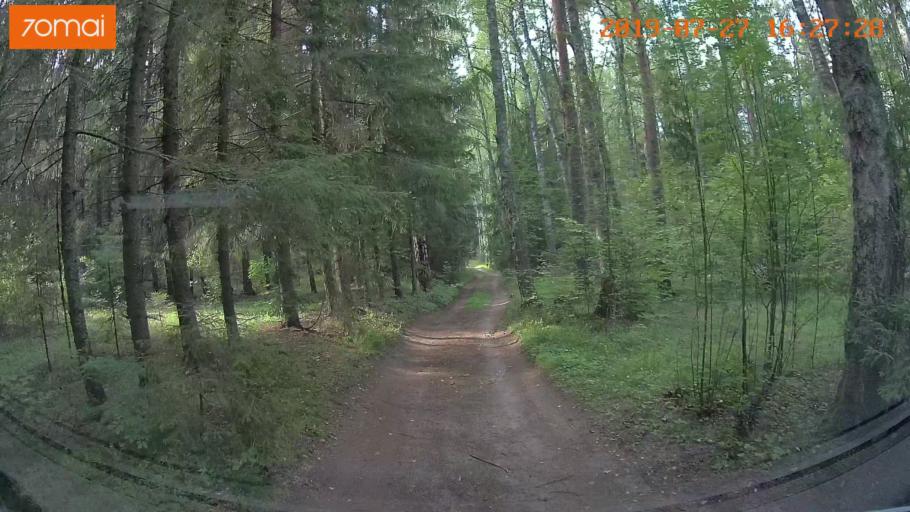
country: RU
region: Ivanovo
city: Novo-Talitsy
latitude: 57.0925
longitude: 40.8531
